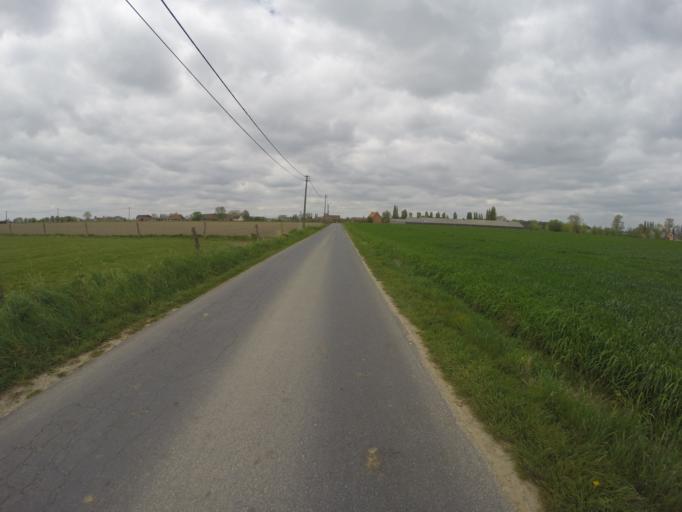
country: BE
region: Flanders
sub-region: Provincie West-Vlaanderen
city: Ruiselede
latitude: 51.0305
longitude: 3.4527
